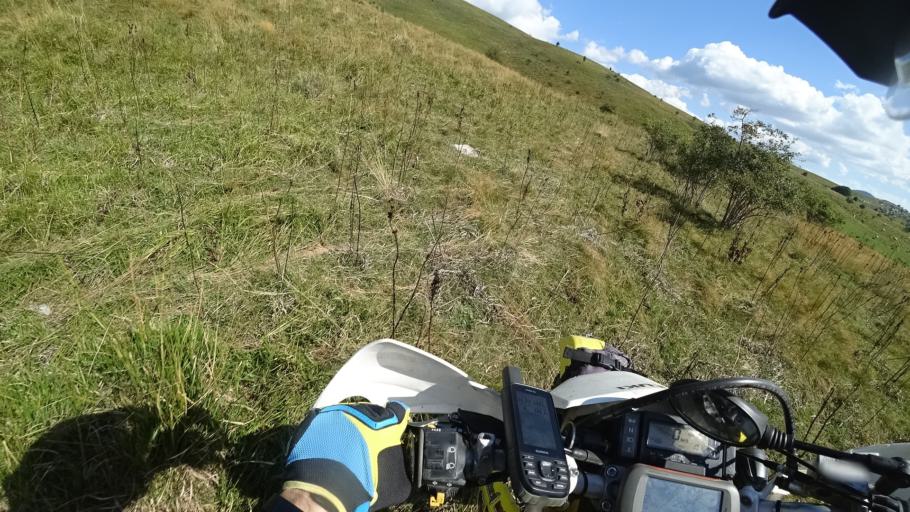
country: HR
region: Zadarska
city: Gracac
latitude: 44.4014
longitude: 16.0092
